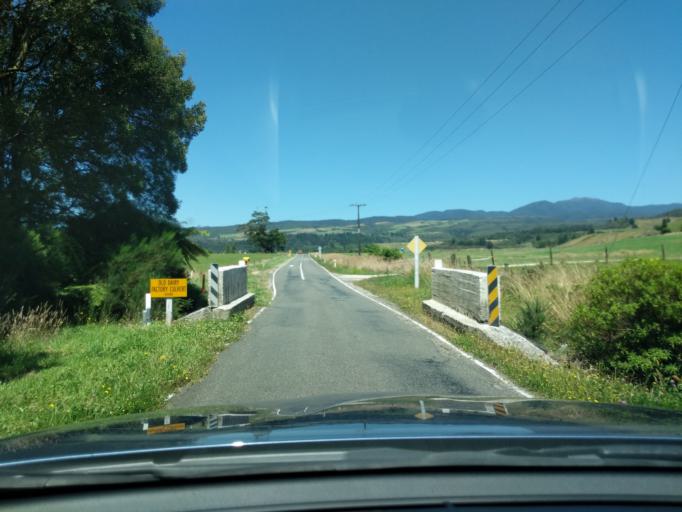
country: NZ
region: Tasman
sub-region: Tasman District
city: Takaka
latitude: -40.7275
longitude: 172.6092
